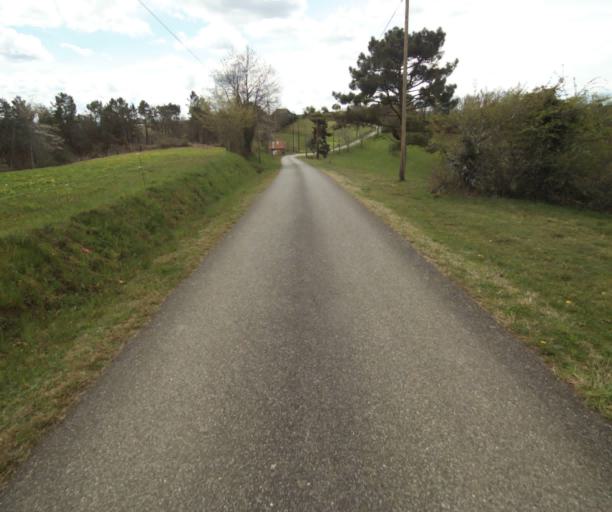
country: FR
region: Limousin
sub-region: Departement de la Correze
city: Sainte-Fortunade
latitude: 45.1928
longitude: 1.8557
